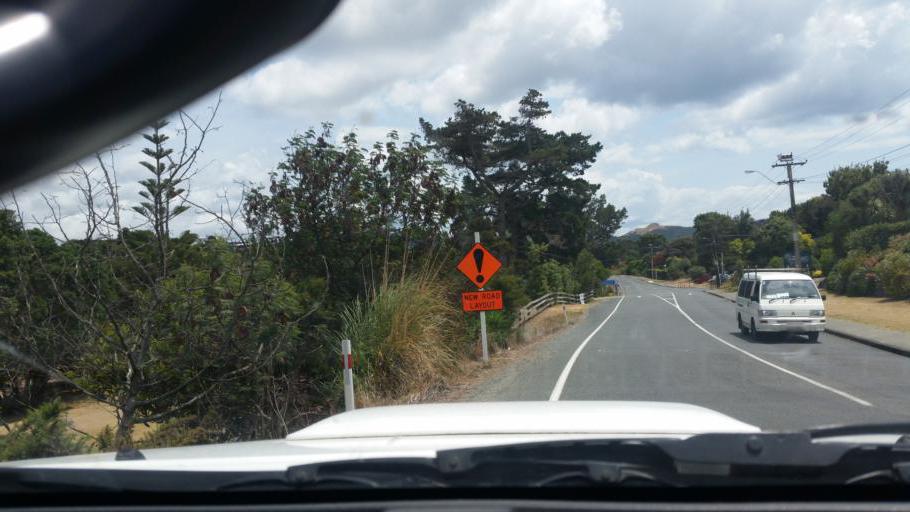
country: NZ
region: Auckland
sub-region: Auckland
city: Wellsford
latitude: -36.0966
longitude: 174.5863
